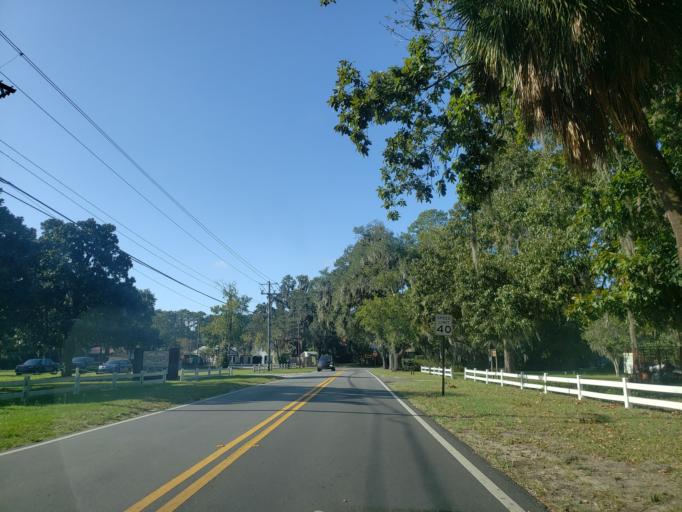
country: US
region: Georgia
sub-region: Chatham County
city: Montgomery
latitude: 31.9448
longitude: -81.1099
